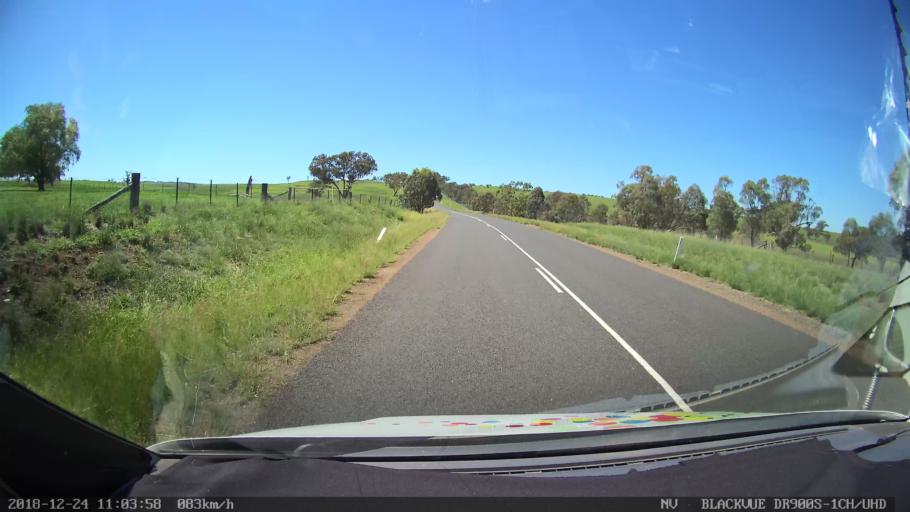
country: AU
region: New South Wales
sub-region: Upper Hunter Shire
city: Merriwa
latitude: -32.1033
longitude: 150.3694
